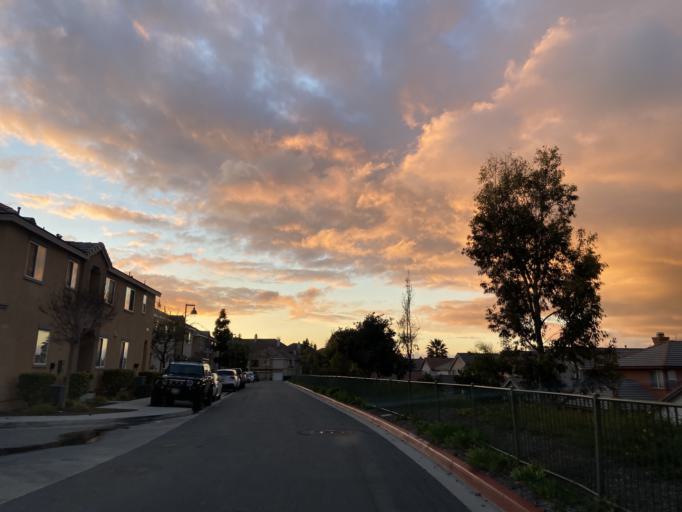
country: US
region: California
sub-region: San Diego County
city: Bonita
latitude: 32.6280
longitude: -116.9723
